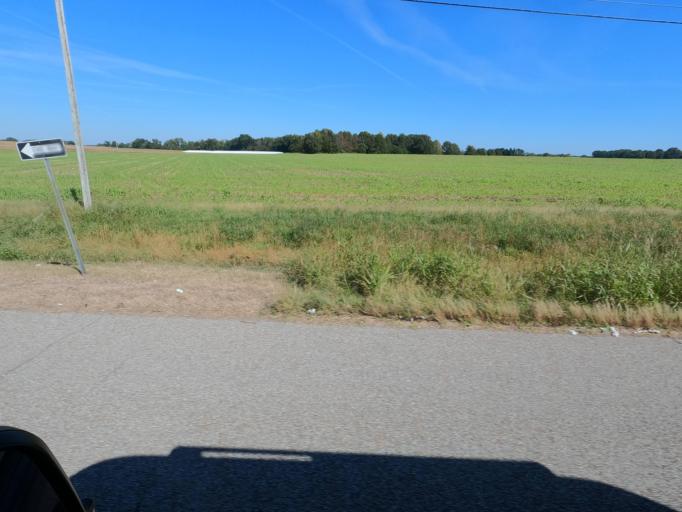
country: US
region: Tennessee
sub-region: Crockett County
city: Bells
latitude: 35.7364
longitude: -89.0777
